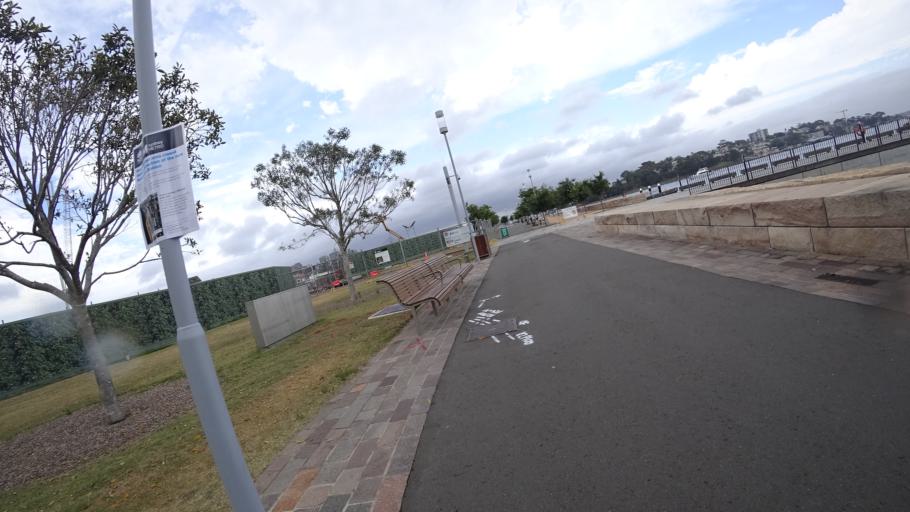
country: AU
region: New South Wales
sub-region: Leichhardt
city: Balmain East
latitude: -33.8595
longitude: 151.2018
